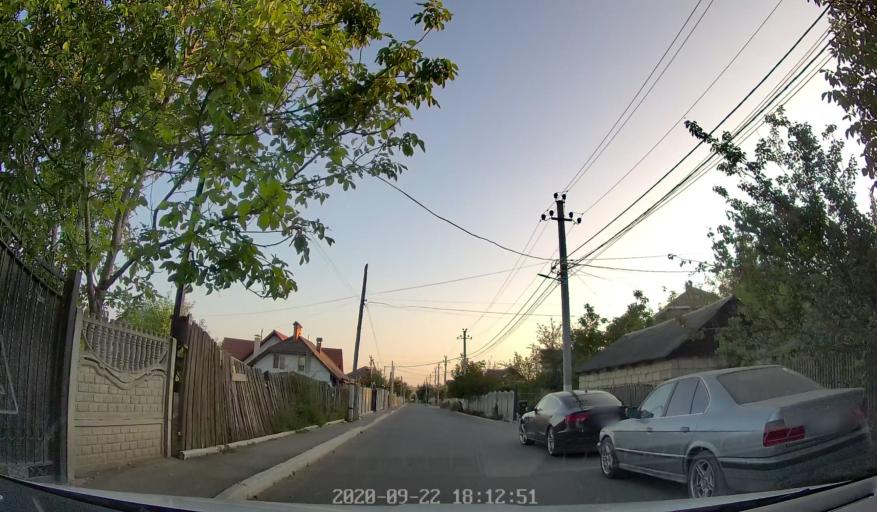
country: MD
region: Laloveni
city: Ialoveni
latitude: 46.9468
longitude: 28.7901
